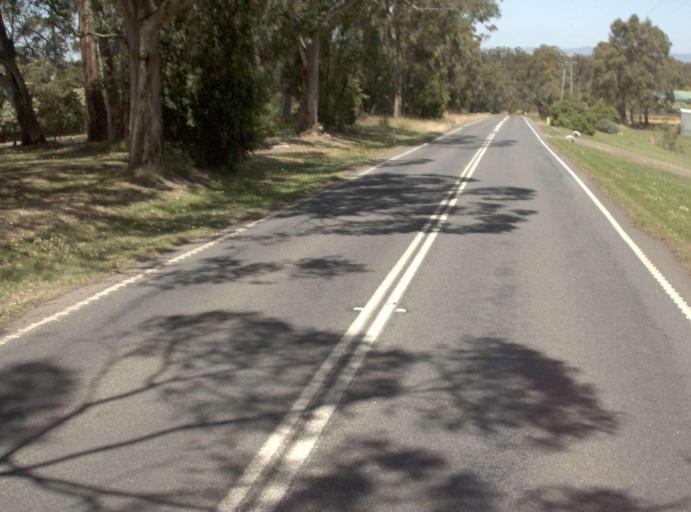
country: AU
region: Victoria
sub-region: Baw Baw
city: Warragul
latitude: -38.0382
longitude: 145.9511
